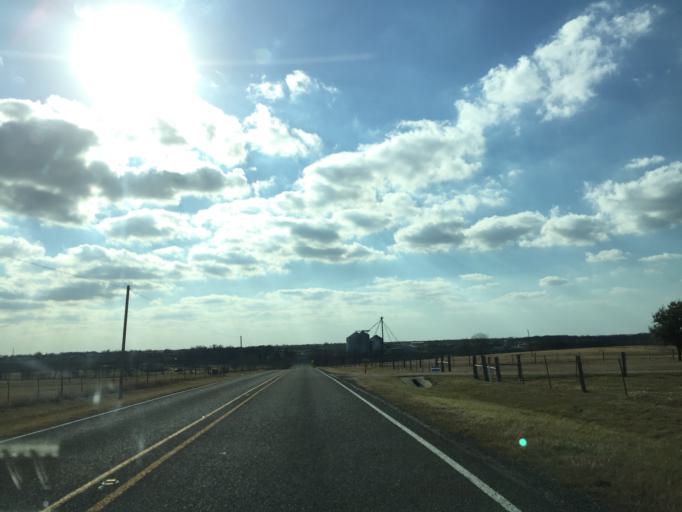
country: US
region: Texas
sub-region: Williamson County
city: Taylor
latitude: 30.6384
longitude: -97.4251
